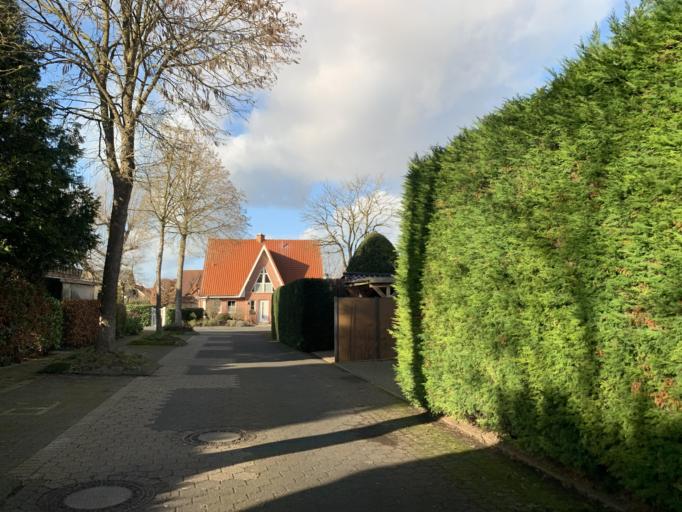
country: DE
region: North Rhine-Westphalia
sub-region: Regierungsbezirk Munster
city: Havixbeck
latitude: 51.9665
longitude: 7.4253
